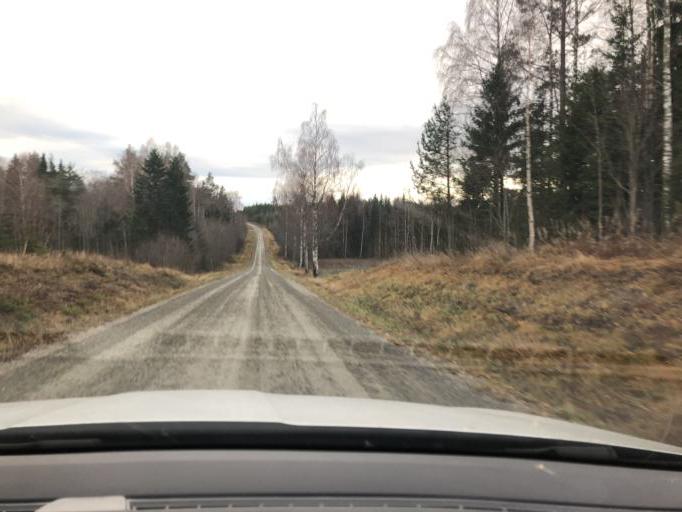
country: SE
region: Gaevleborg
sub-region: Hudiksvalls Kommun
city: Sorforsa
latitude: 61.6535
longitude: 16.9266
